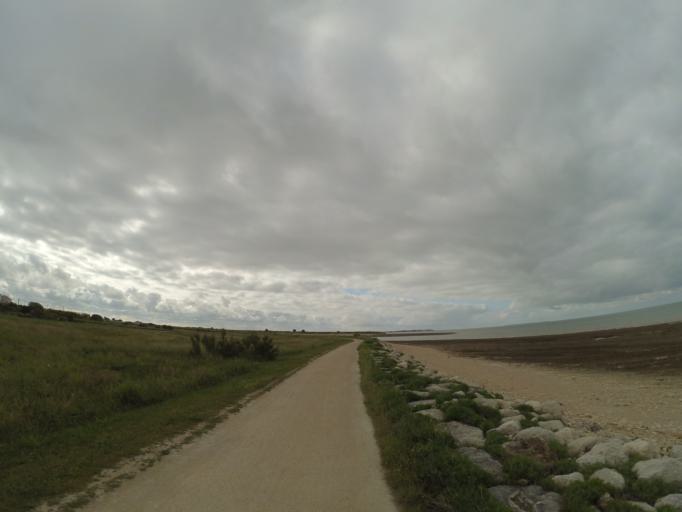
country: FR
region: Poitou-Charentes
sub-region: Departement de la Charente-Maritime
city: La Rochelle
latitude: 46.1352
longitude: -1.1516
